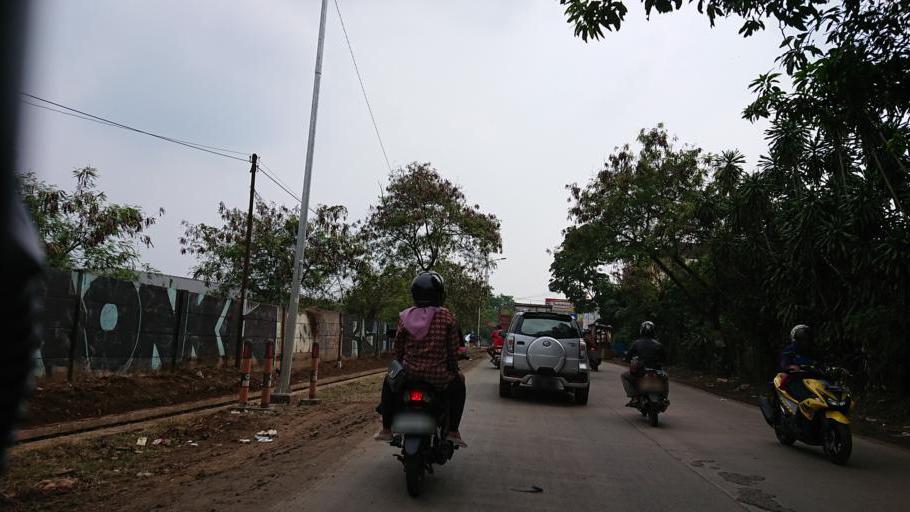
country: ID
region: West Java
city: Serpong
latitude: -6.3786
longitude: 106.6809
